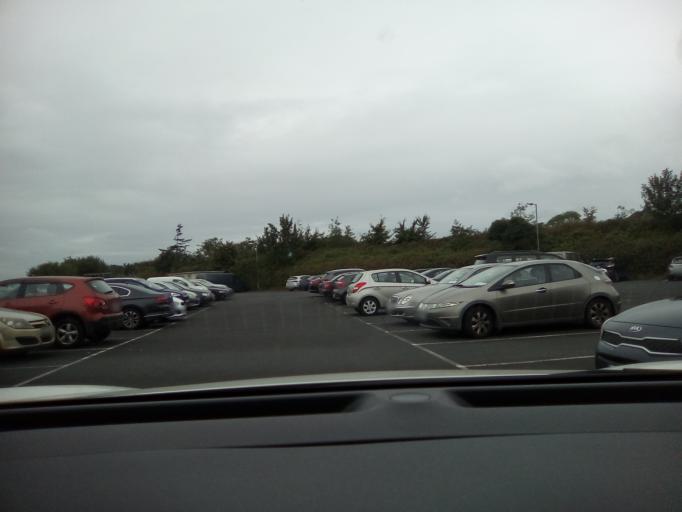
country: IE
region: Leinster
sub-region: Kildare
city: Leixlip
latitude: 53.3559
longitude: -6.4899
